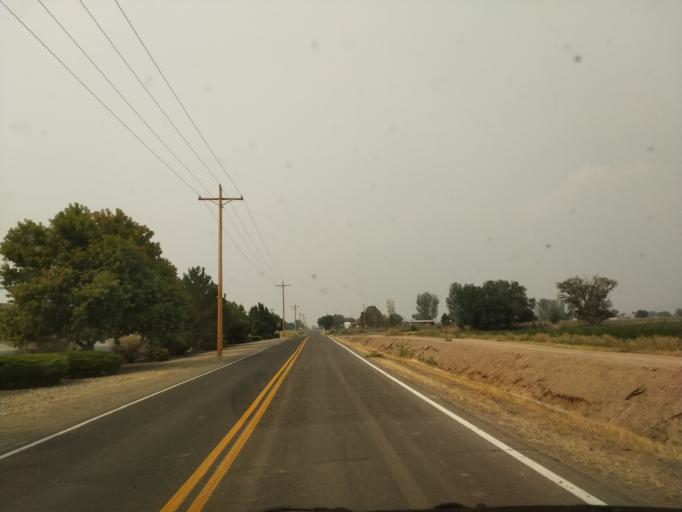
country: US
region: Colorado
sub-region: Mesa County
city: Fruitvale
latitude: 39.0323
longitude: -108.4967
